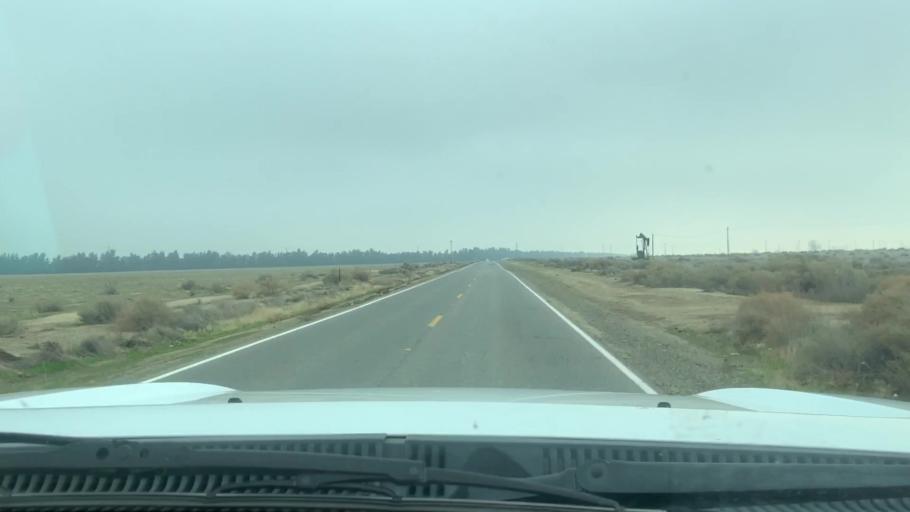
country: US
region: California
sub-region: Kern County
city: Lost Hills
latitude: 35.5338
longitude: -119.7680
